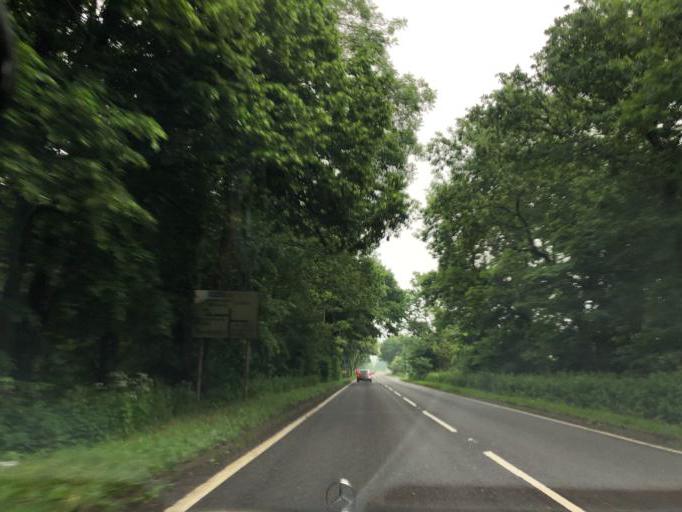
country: GB
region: England
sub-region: Warwickshire
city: Wellesbourne Mountford
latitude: 52.2332
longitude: -1.5499
